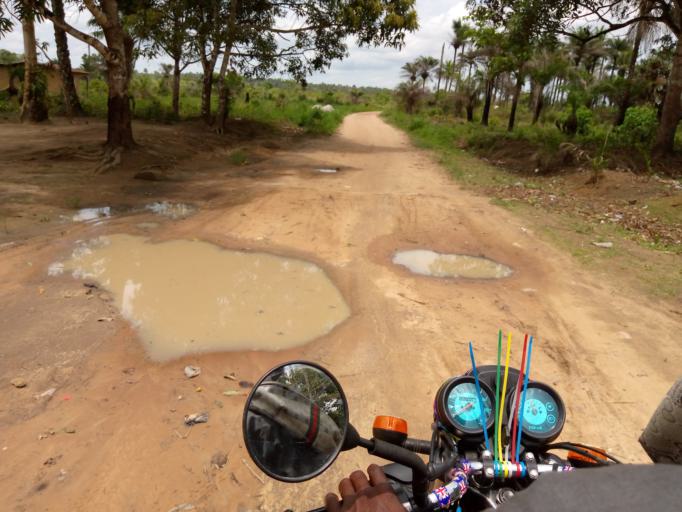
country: SL
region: Western Area
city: Waterloo
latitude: 8.3296
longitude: -12.9407
